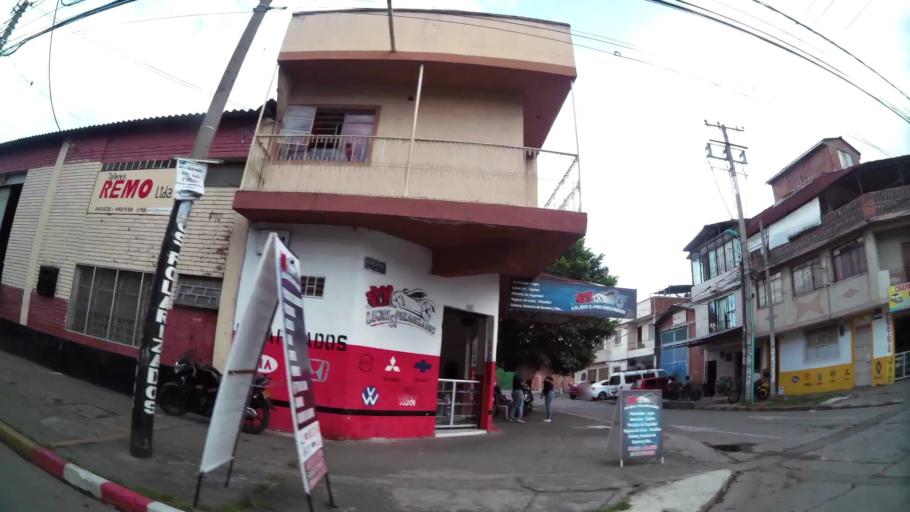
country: CO
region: Valle del Cauca
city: Cali
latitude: 3.4569
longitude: -76.5162
